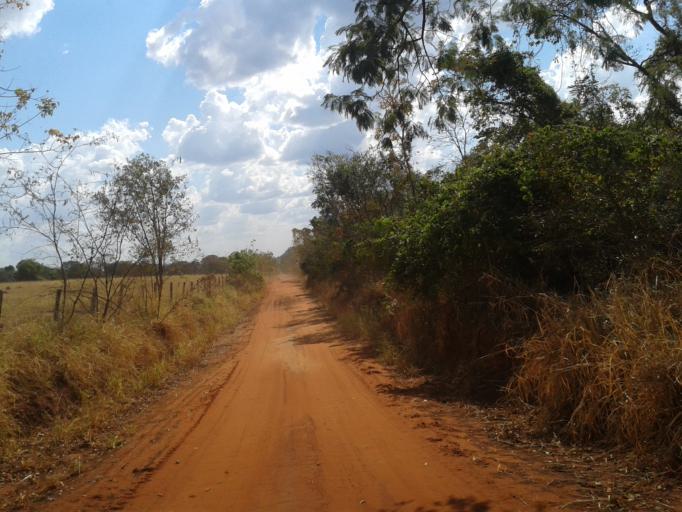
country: BR
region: Minas Gerais
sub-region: Santa Vitoria
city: Santa Vitoria
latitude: -19.1994
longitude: -49.9075
